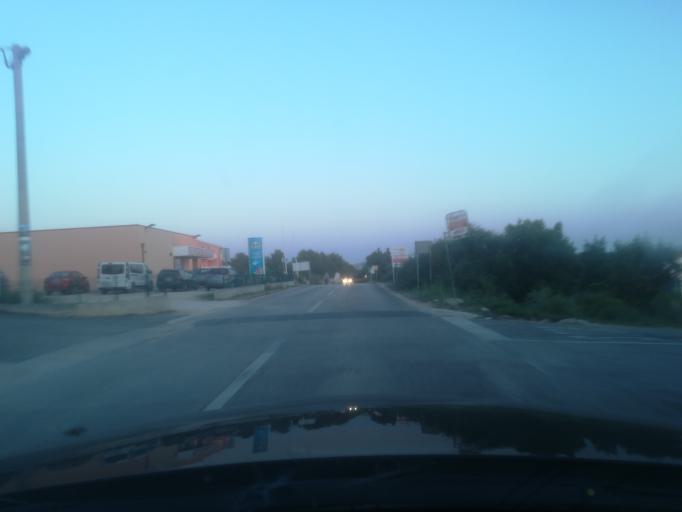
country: HR
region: Primorsko-Goranska
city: Banjol
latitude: 44.7373
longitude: 14.8027
